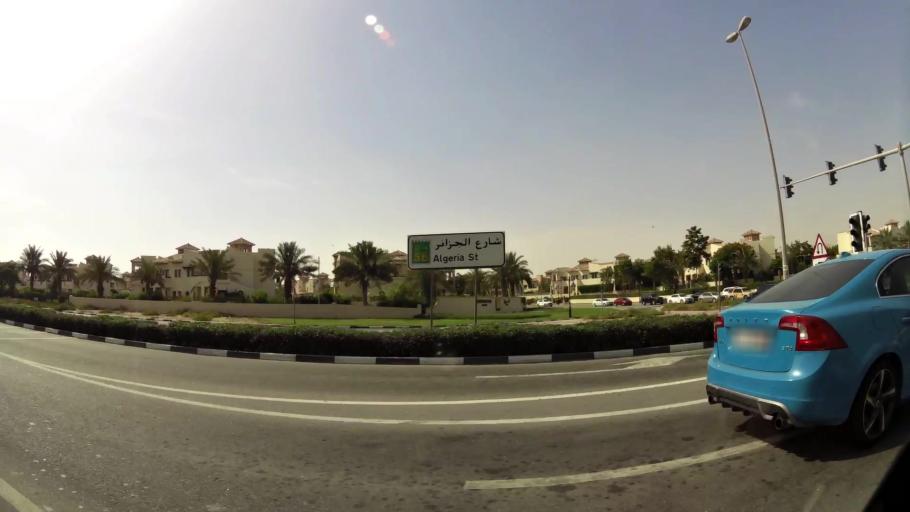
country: AE
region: Ash Shariqah
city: Sharjah
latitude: 25.2129
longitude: 55.4237
